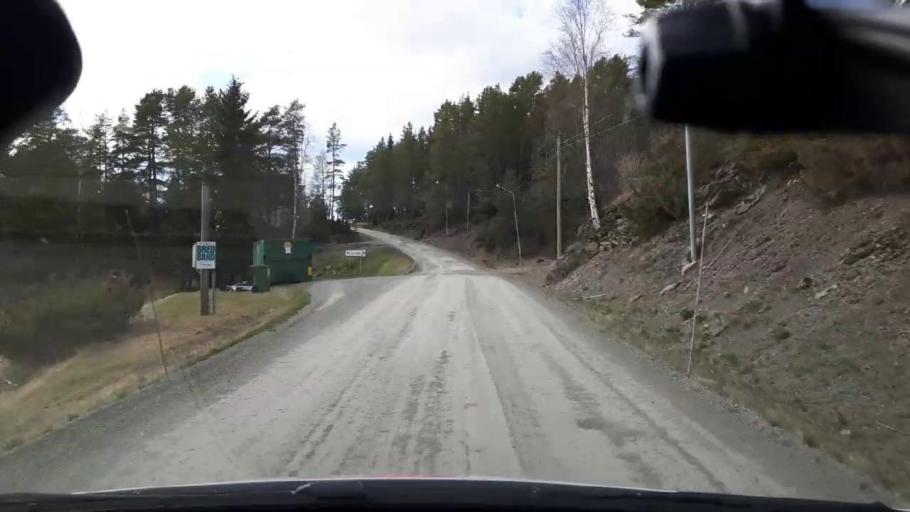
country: SE
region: Jaemtland
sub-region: OEstersunds Kommun
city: Brunflo
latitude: 62.9559
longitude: 14.6477
